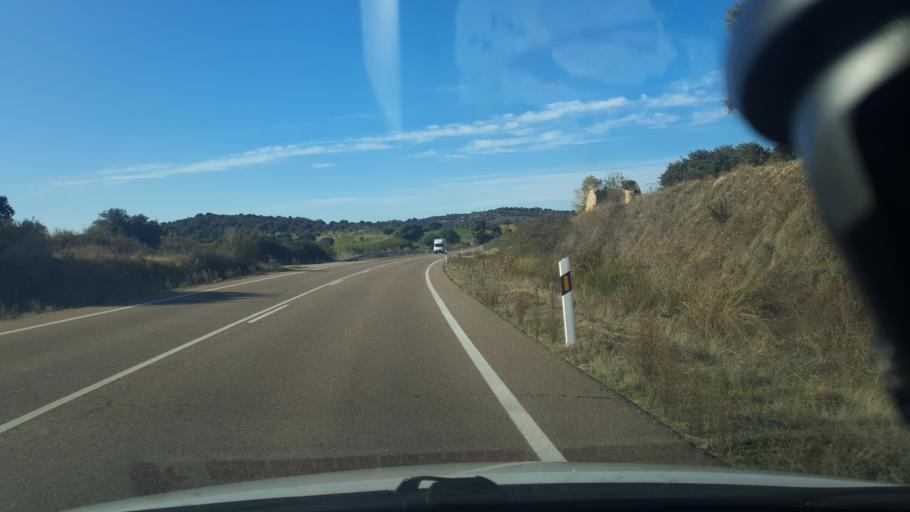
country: ES
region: Castille and Leon
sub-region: Provincia de Avila
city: Poyales del Hoyo
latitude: 40.1601
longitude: -5.1482
